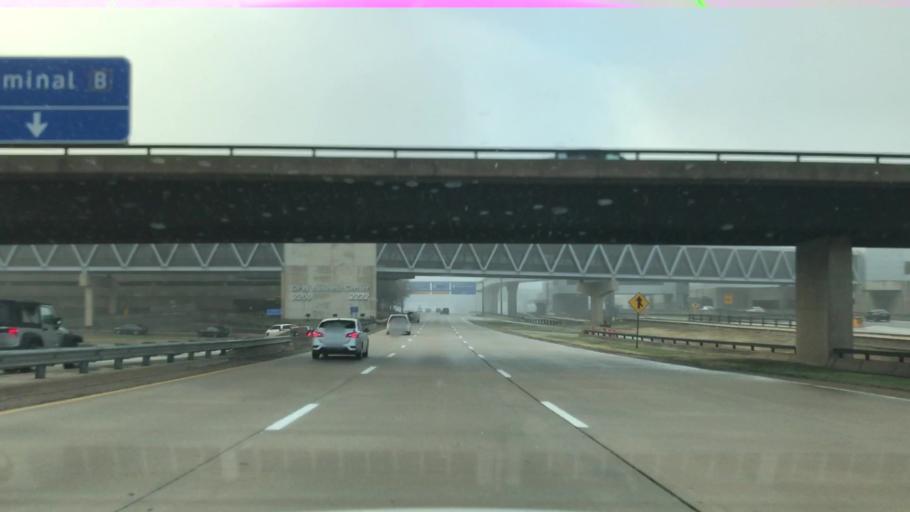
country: US
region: Texas
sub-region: Tarrant County
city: Grapevine
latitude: 32.9038
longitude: -97.0410
